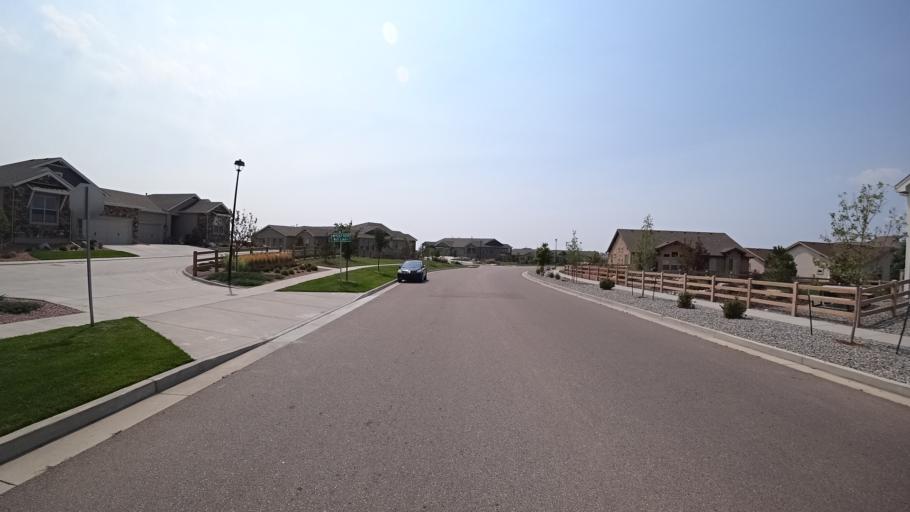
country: US
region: Colorado
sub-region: El Paso County
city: Black Forest
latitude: 38.9666
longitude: -104.7137
